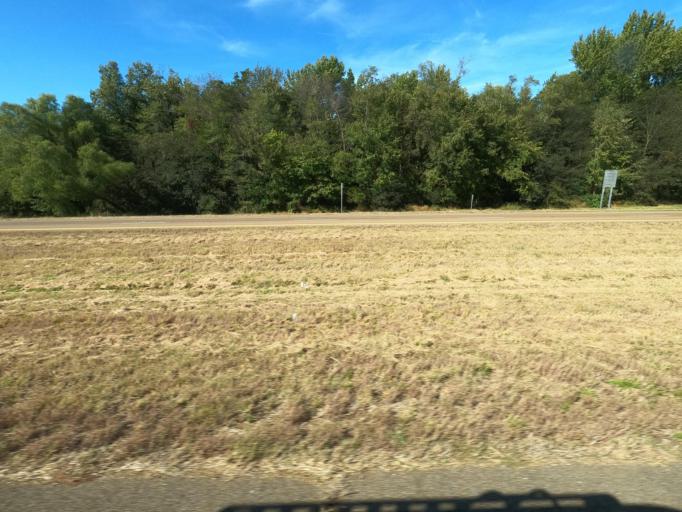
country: US
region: Tennessee
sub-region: Obion County
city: South Fulton
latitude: 36.4838
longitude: -88.9371
